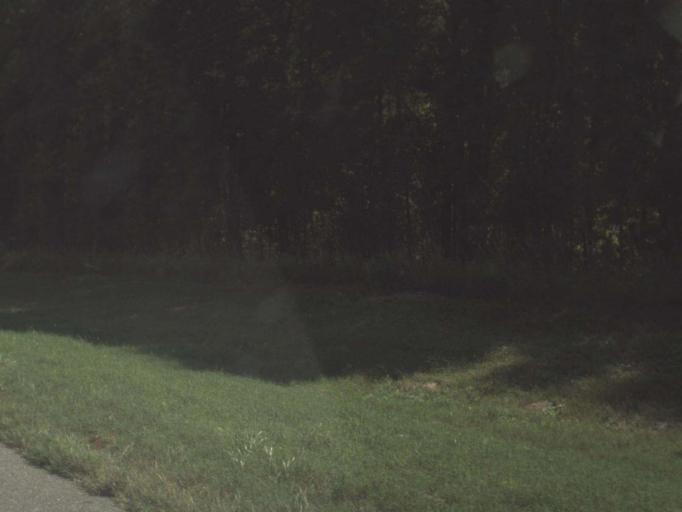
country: US
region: Alabama
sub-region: Houston County
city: Cottonwood
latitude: 30.9447
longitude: -85.2767
